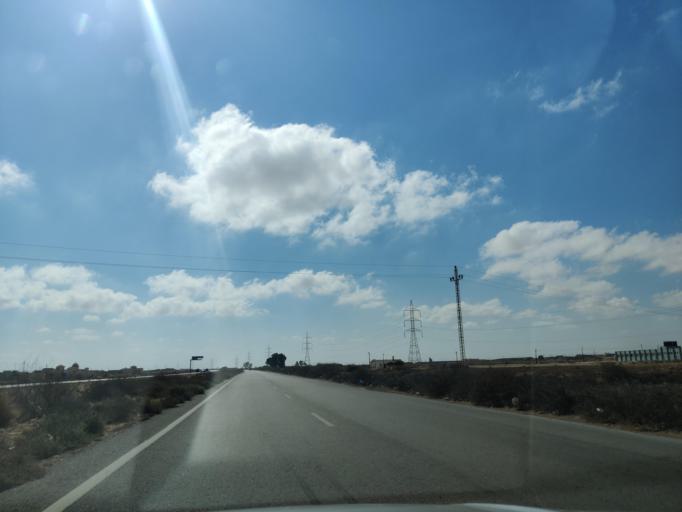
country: EG
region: Muhafazat Matruh
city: Al `Alamayn
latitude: 31.0552
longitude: 28.2581
